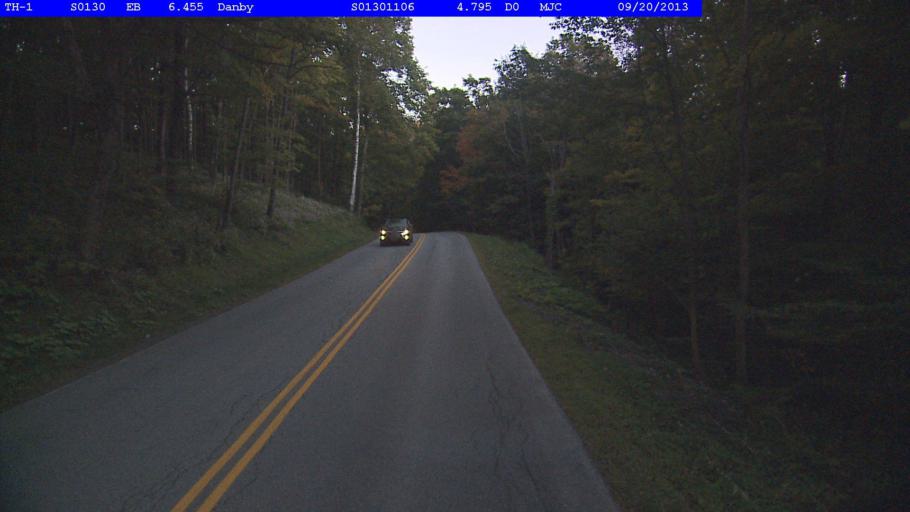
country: US
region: Vermont
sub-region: Bennington County
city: Manchester Center
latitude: 43.3467
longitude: -73.0479
